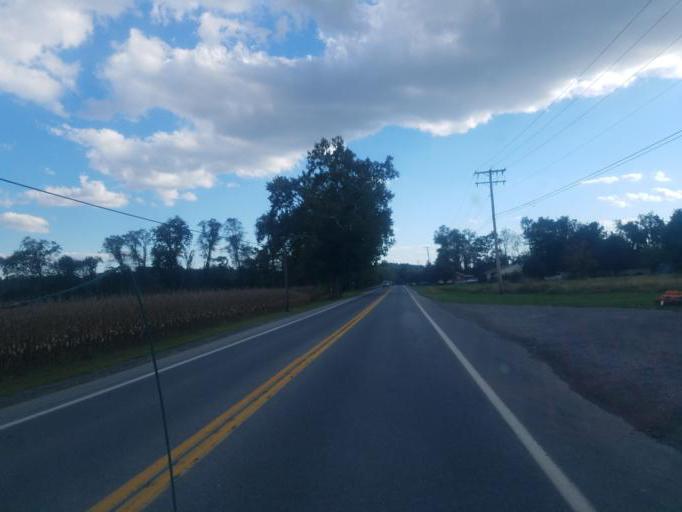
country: US
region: Pennsylvania
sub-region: Dauphin County
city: Middletown
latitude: 40.1416
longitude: -76.7162
